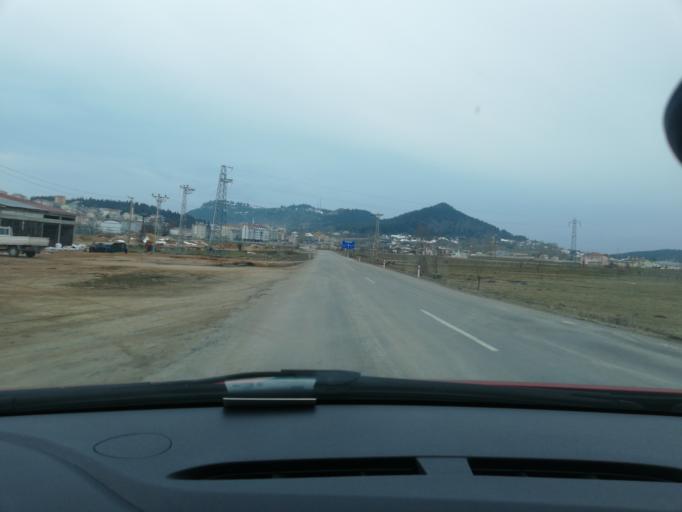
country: TR
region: Kastamonu
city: Agli
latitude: 41.6895
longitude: 33.5617
